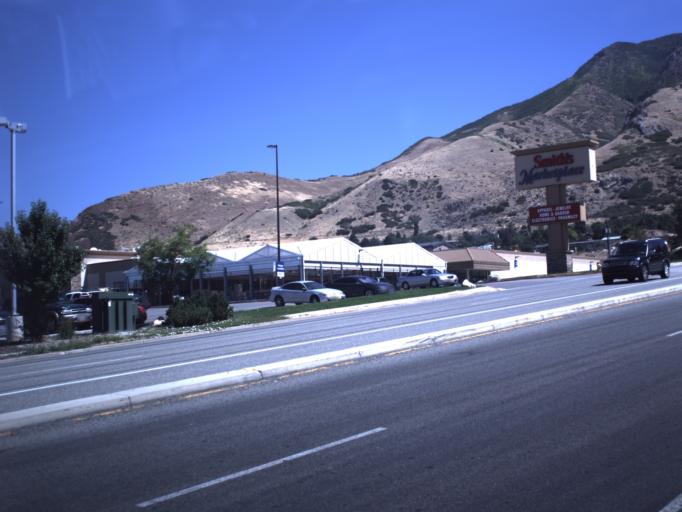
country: US
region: Utah
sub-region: Salt Lake County
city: East Millcreek
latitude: 40.6998
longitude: -111.8003
